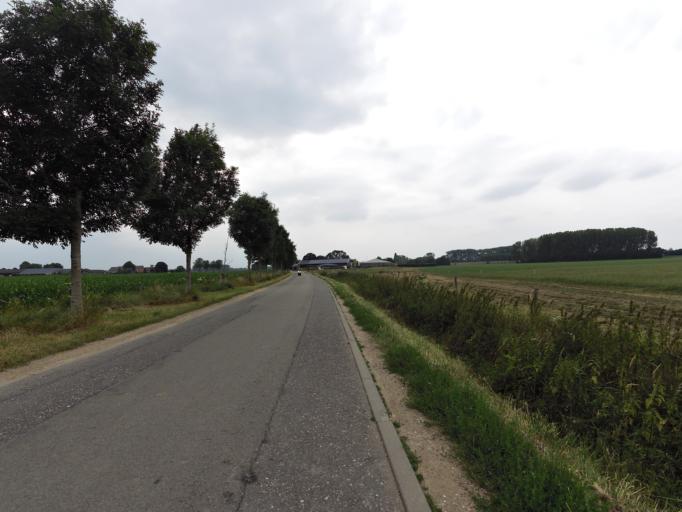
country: DE
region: North Rhine-Westphalia
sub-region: Regierungsbezirk Dusseldorf
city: Kranenburg
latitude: 51.8582
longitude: 6.0253
